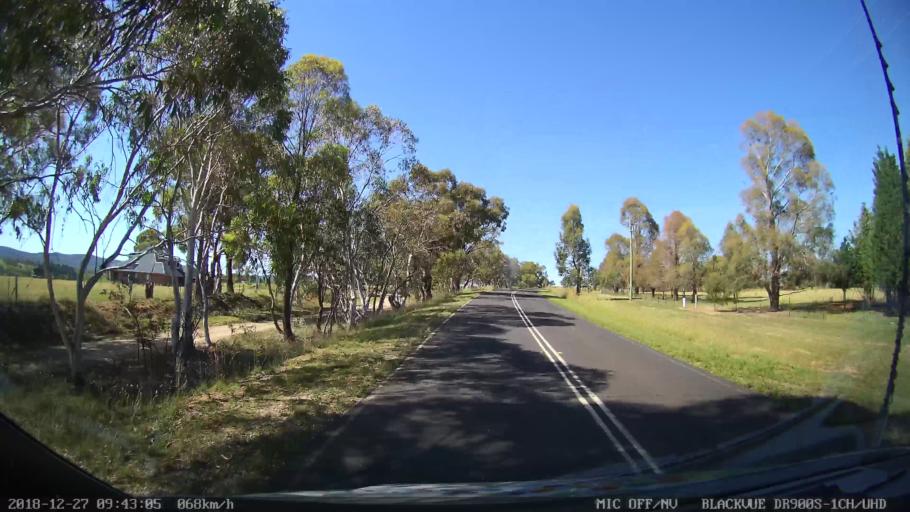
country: AU
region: New South Wales
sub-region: Lithgow
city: Portland
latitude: -33.3032
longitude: 150.0038
